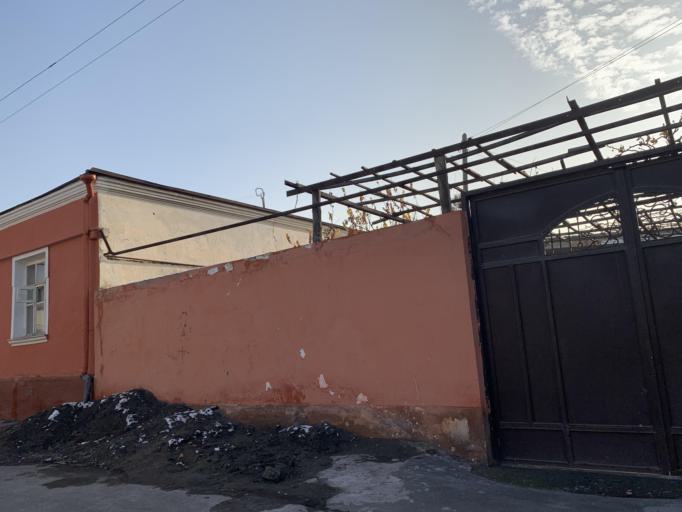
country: UZ
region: Fergana
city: Qo`qon
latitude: 40.5424
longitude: 70.9318
